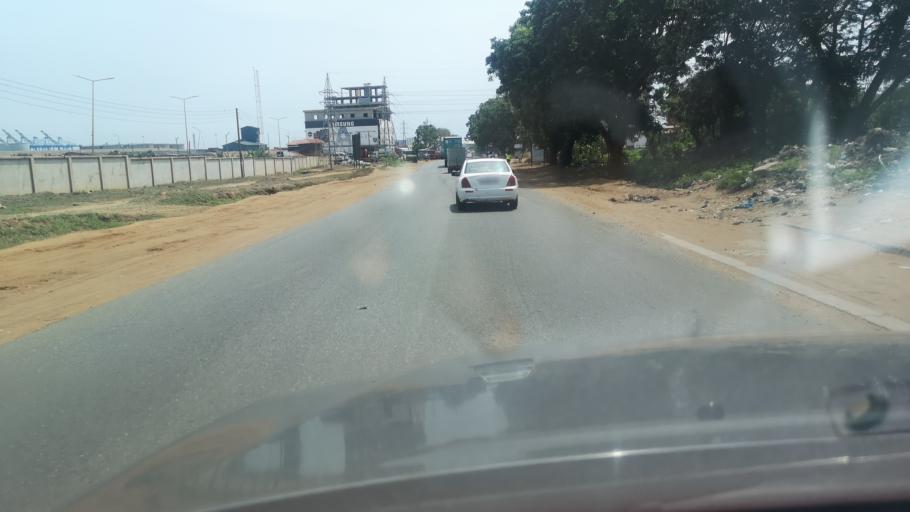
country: GH
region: Greater Accra
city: Tema
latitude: 5.6330
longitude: -0.0033
